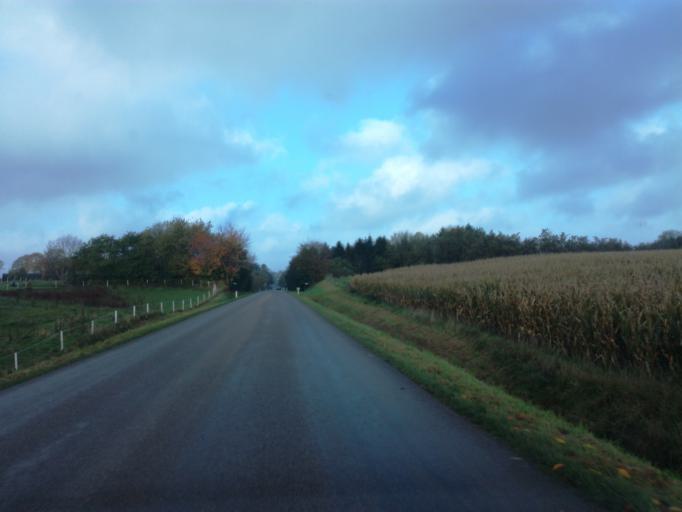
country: DK
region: South Denmark
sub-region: Vejle Kommune
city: Brejning
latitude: 55.6292
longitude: 9.7169
